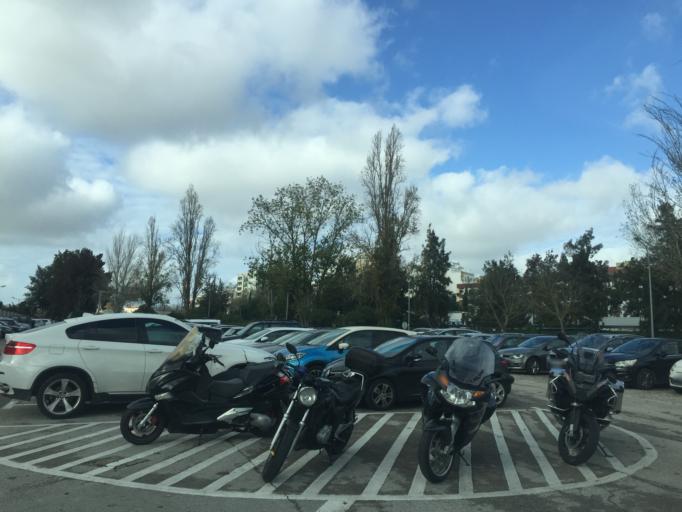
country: PT
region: Lisbon
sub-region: Amadora
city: Amadora
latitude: 38.7393
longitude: -9.2155
